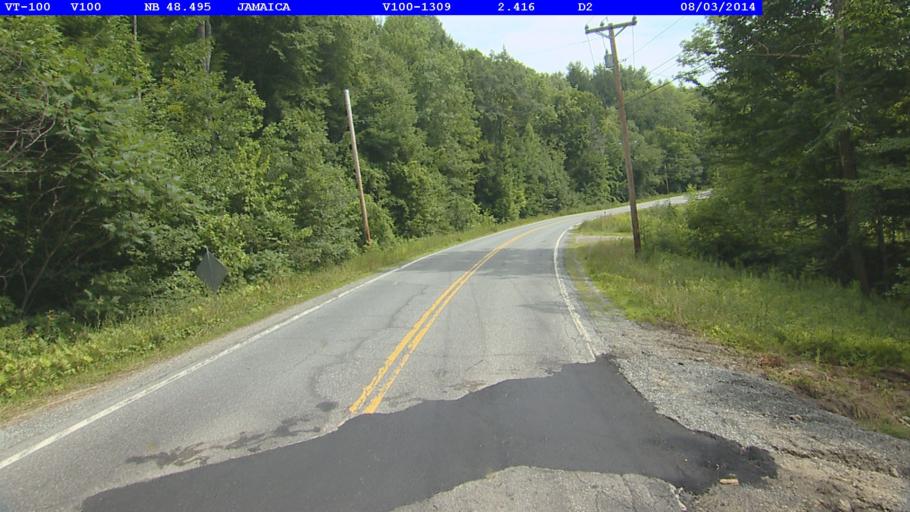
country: US
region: Vermont
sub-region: Windham County
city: Newfane
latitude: 43.0679
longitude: -72.7523
